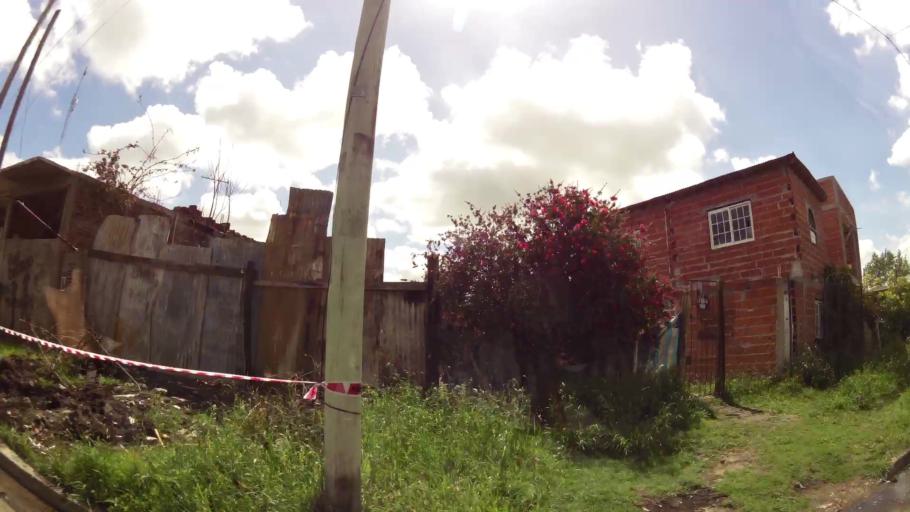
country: AR
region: Buenos Aires
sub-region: Partido de Quilmes
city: Quilmes
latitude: -34.8380
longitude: -58.1794
